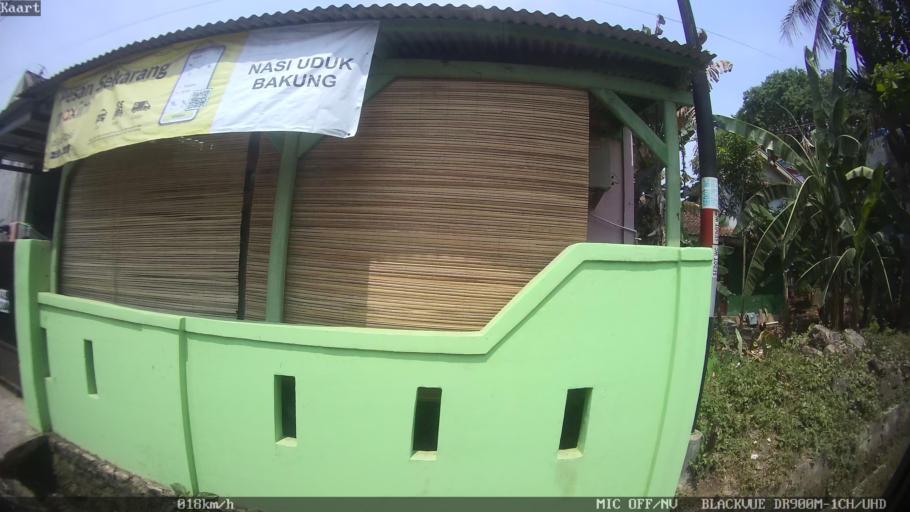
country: ID
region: Lampung
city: Bandarlampung
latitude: -5.4516
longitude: 105.2510
